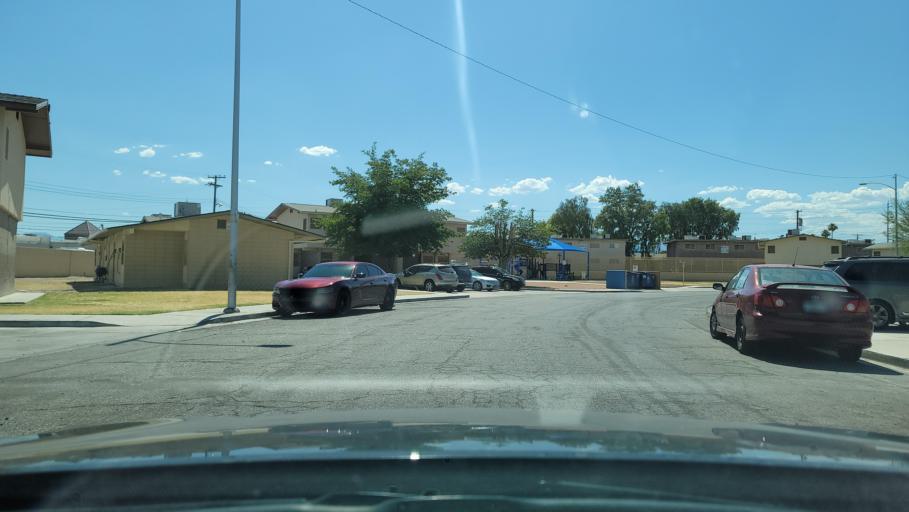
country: US
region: Nevada
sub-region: Clark County
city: Las Vegas
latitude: 36.1899
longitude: -115.1536
